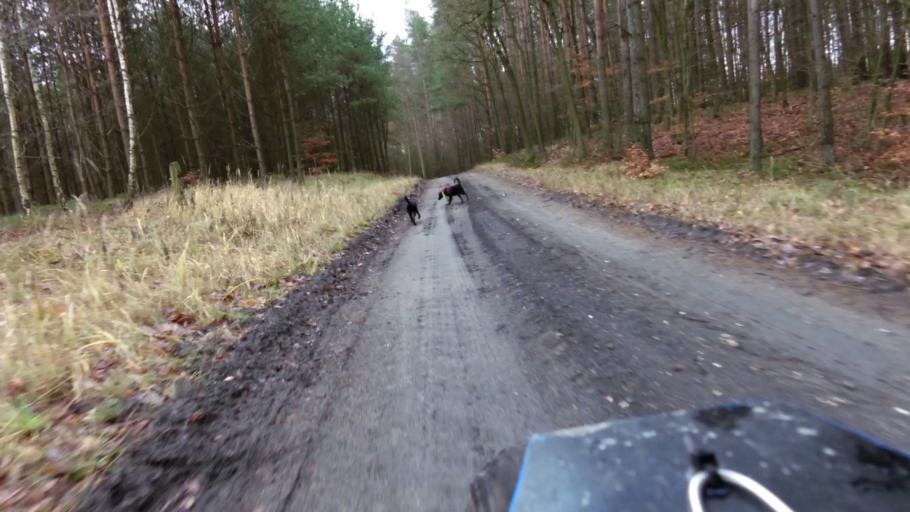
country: PL
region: Lubusz
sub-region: Powiat gorzowski
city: Bogdaniec
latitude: 52.6942
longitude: 15.0329
